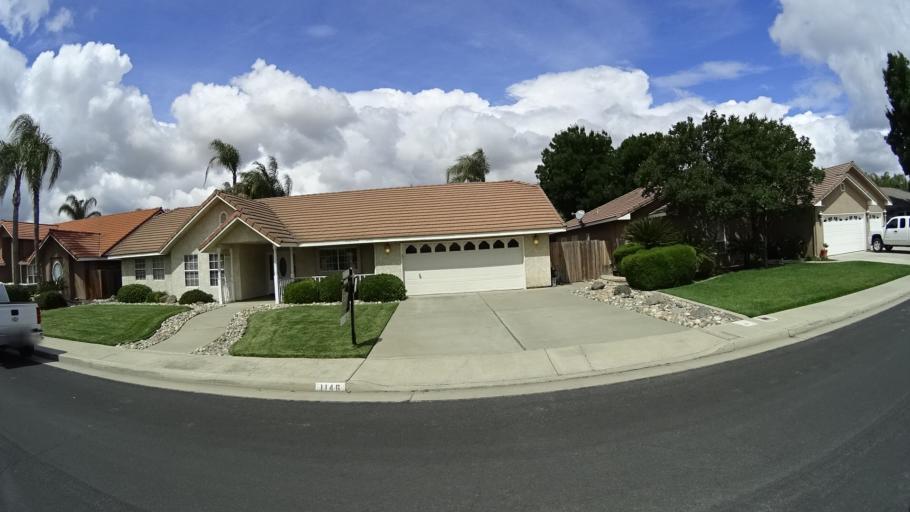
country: US
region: California
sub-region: Kings County
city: Hanford
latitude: 36.3367
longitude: -119.6669
